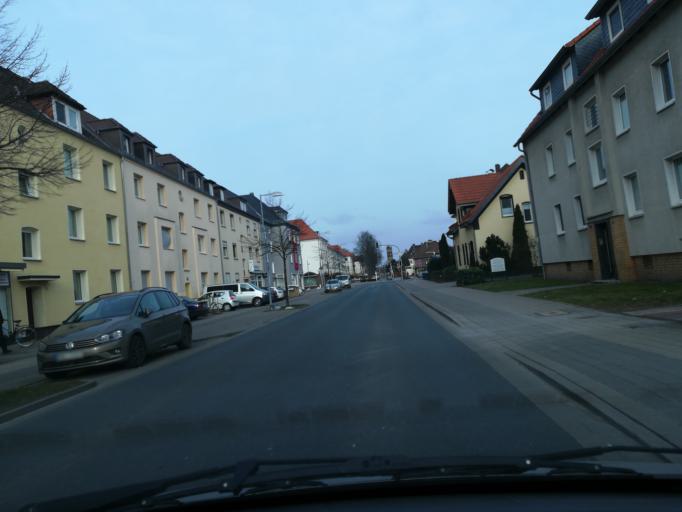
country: DE
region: Lower Saxony
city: Seelze
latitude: 52.3960
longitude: 9.6354
